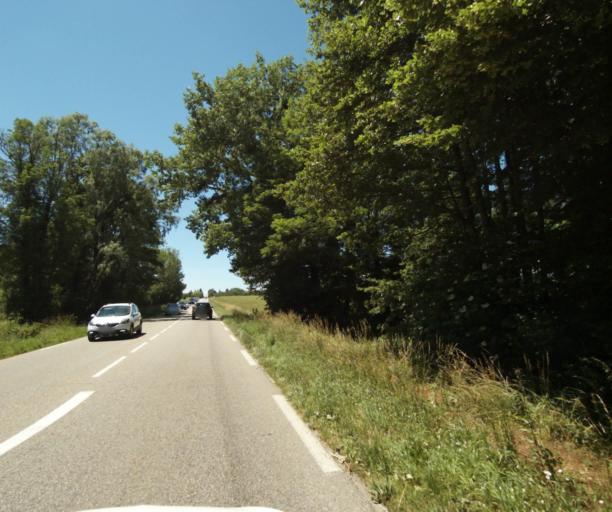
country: FR
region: Rhone-Alpes
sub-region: Departement de la Haute-Savoie
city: Massongy
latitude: 46.3222
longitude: 6.3427
